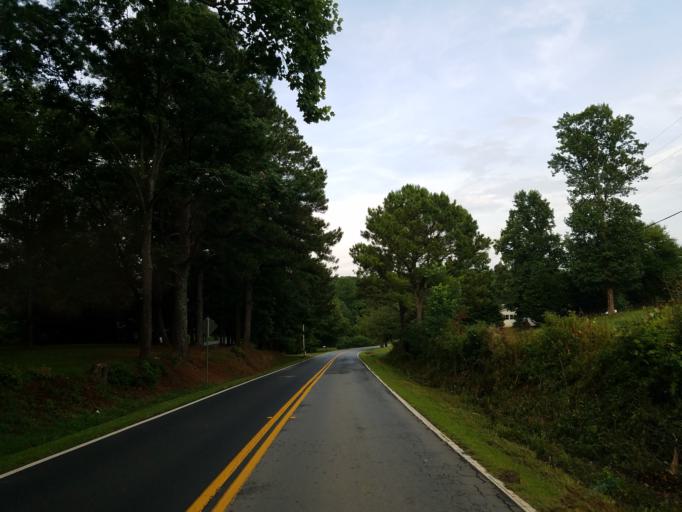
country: US
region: Georgia
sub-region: Pickens County
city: Jasper
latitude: 34.4634
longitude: -84.5249
